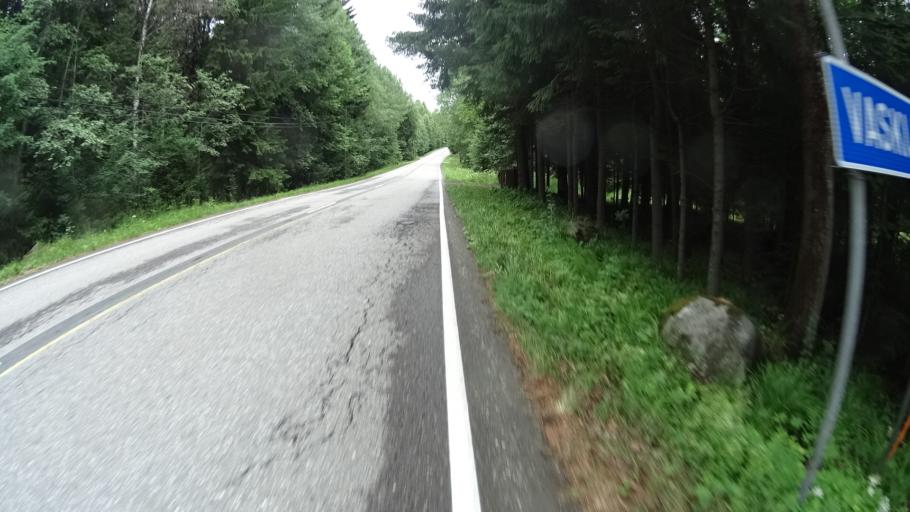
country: FI
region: Uusimaa
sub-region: Helsinki
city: Karkkila
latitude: 60.5754
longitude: 24.3253
